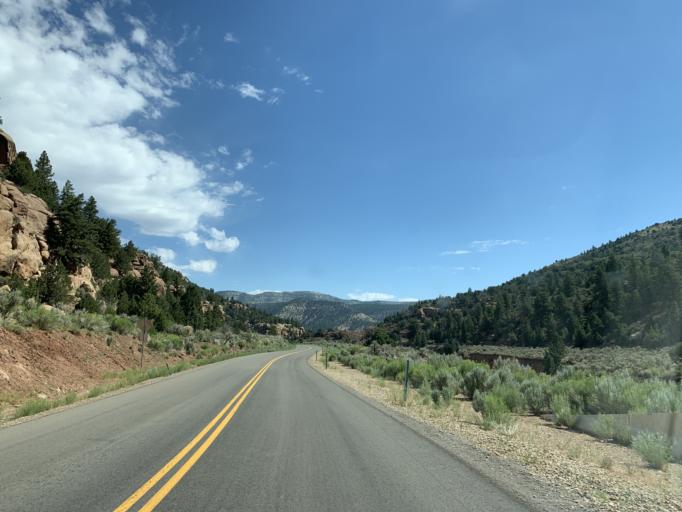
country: US
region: Utah
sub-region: Carbon County
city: East Carbon City
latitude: 39.7565
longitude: -110.5281
